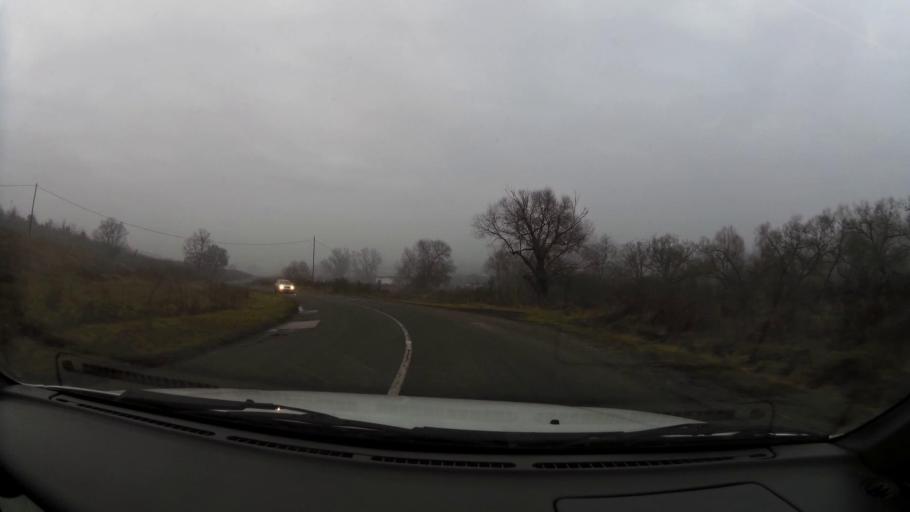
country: HU
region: Borsod-Abauj-Zemplen
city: Rudabanya
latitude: 48.3613
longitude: 20.6322
